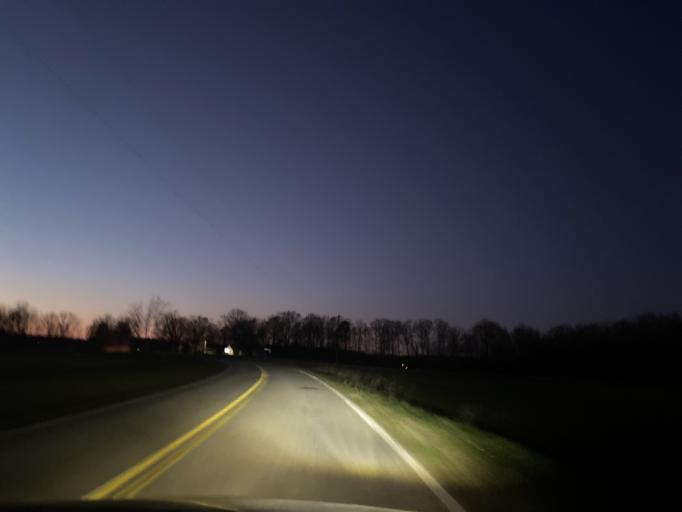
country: US
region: South Carolina
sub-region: Cherokee County
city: Gaffney
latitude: 35.1307
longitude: -81.7074
